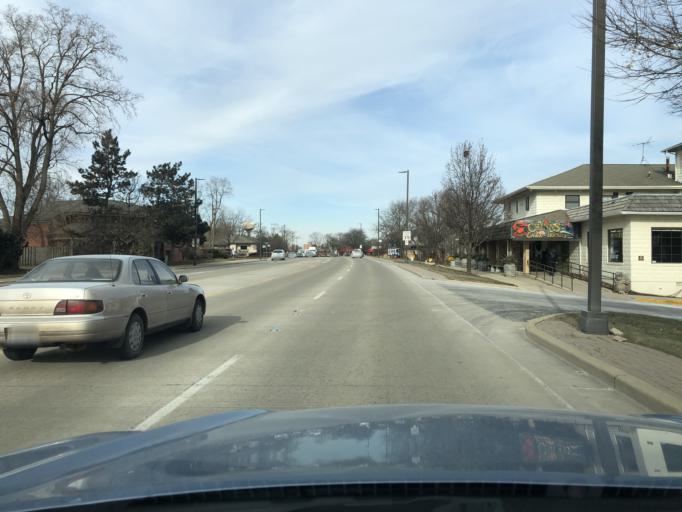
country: US
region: Illinois
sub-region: Cook County
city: Wheeling
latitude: 42.1339
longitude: -87.9024
